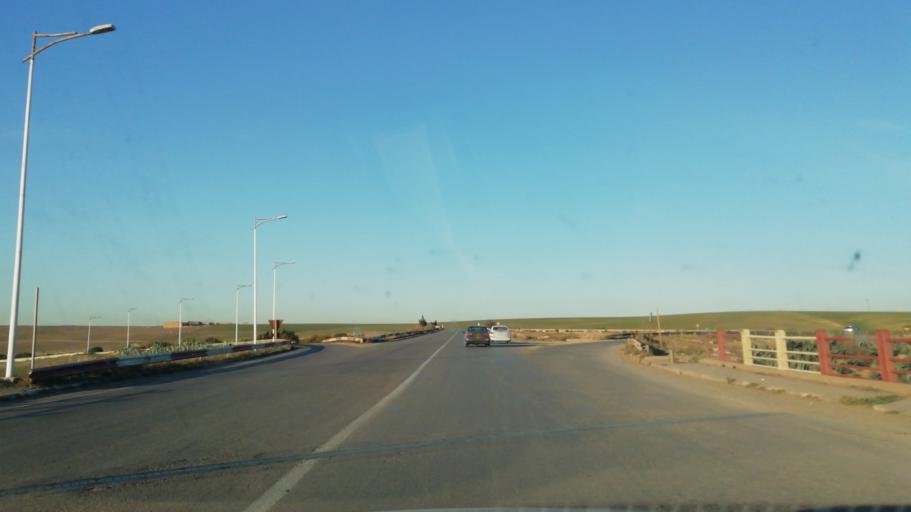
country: DZ
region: Oran
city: Sidi ech Chahmi
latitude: 35.5724
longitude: -0.5570
